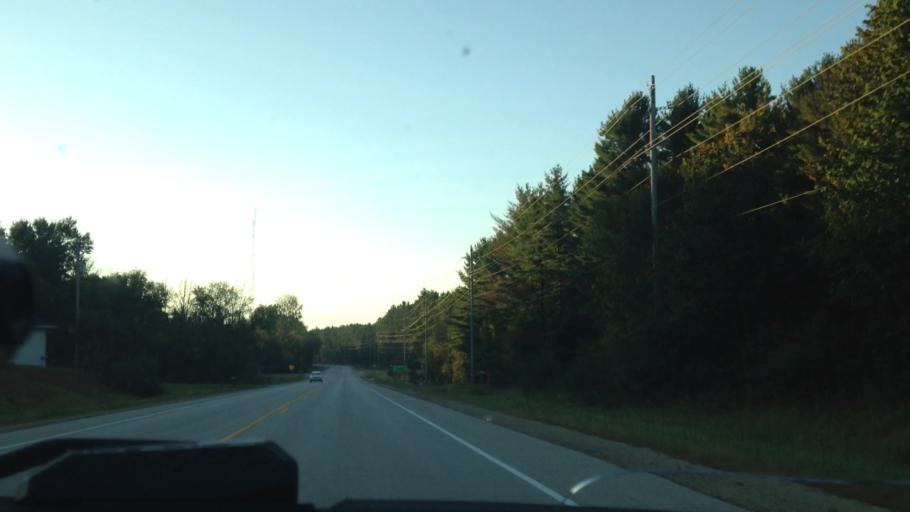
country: US
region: Wisconsin
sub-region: Washington County
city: Newburg
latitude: 43.4136
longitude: -88.0133
